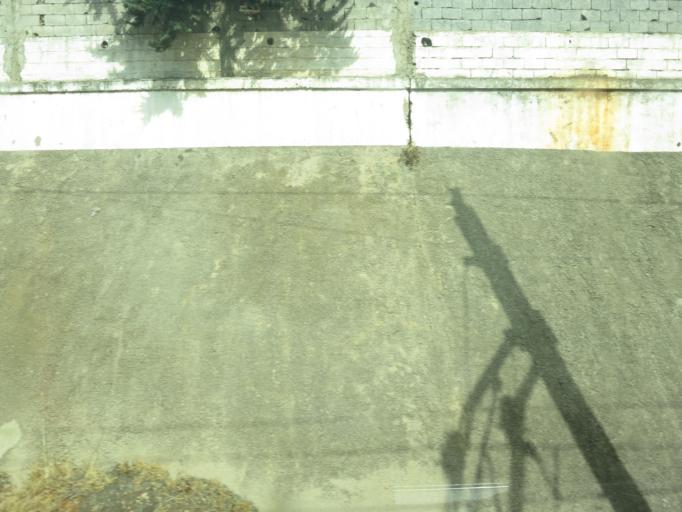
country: MA
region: Rabat-Sale-Zemmour-Zaer
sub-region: Rabat
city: Rabat
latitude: 34.0054
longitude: -6.8520
